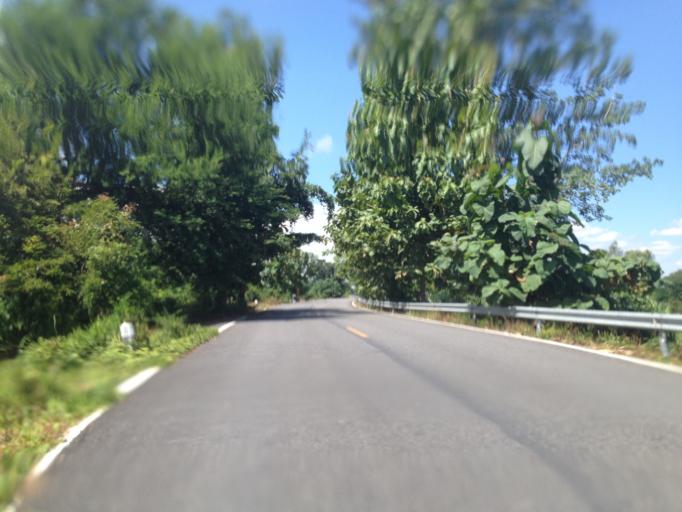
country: TH
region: Chiang Mai
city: San Pa Tong
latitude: 18.6340
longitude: 98.9530
